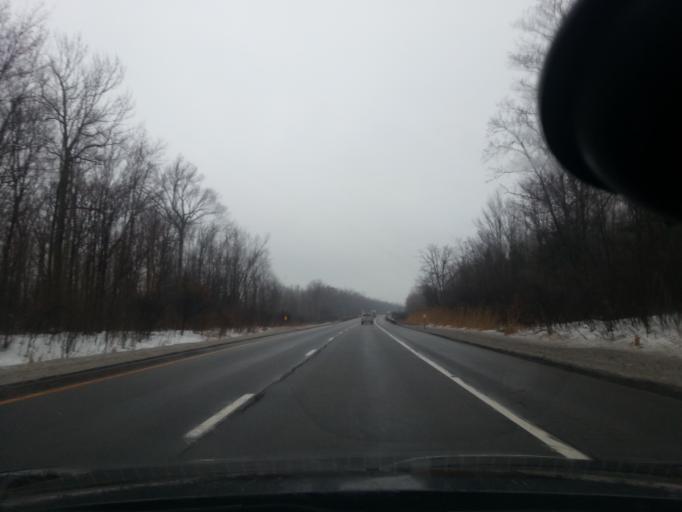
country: US
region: New York
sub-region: Oswego County
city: Pulaski
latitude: 43.6224
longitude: -76.0846
